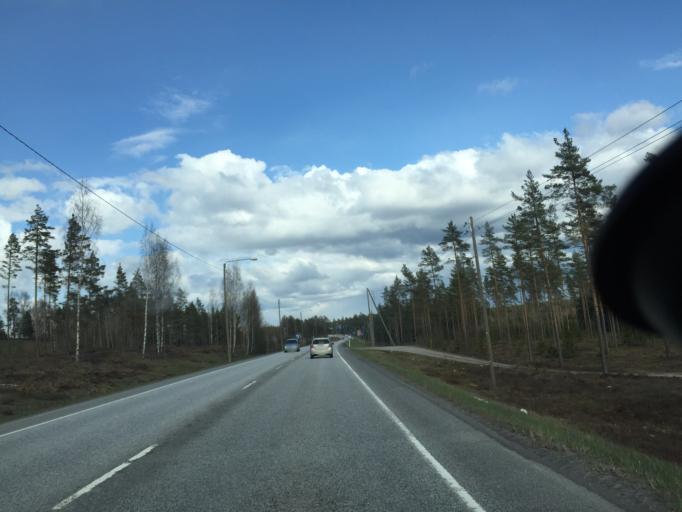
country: FI
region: Uusimaa
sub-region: Raaseporin
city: Pohja
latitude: 60.0141
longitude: 23.5565
